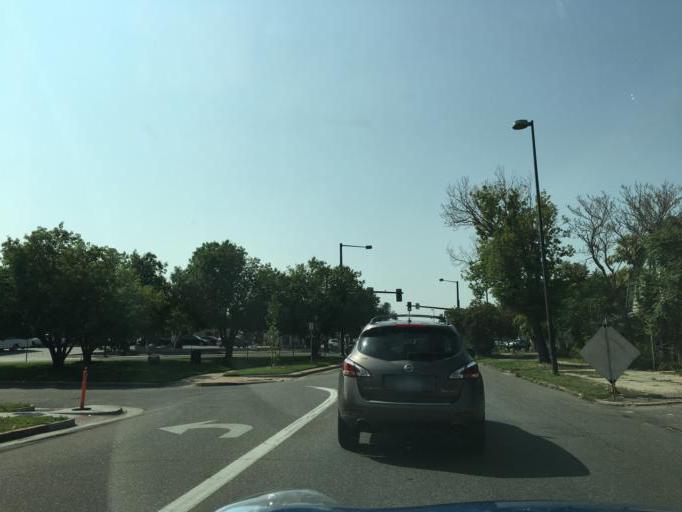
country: US
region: Colorado
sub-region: Denver County
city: Denver
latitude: 39.7672
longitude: -104.9734
